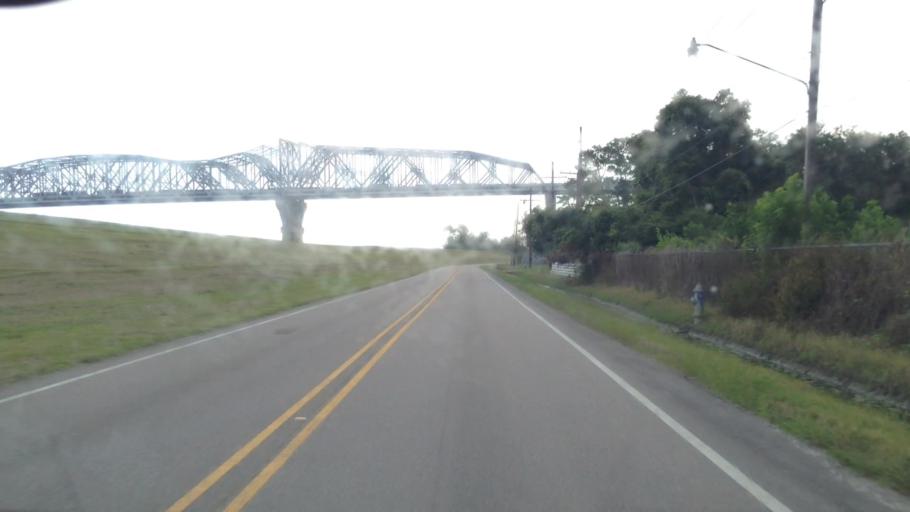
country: US
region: Louisiana
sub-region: Jefferson Parish
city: Bridge City
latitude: 29.9374
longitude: -90.1699
